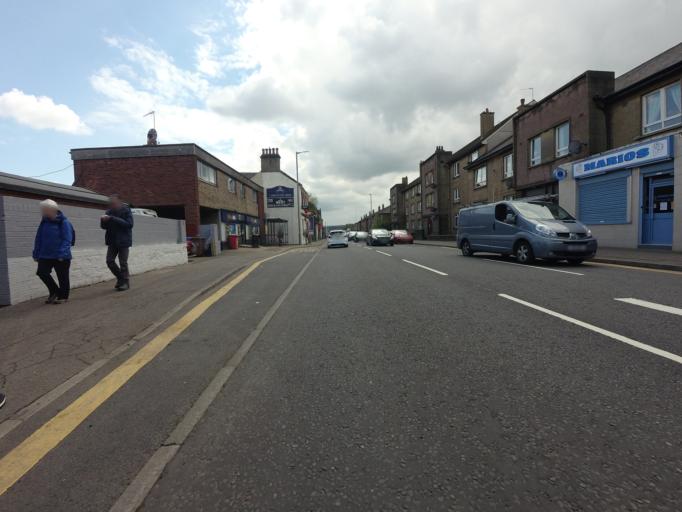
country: GB
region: Scotland
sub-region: Falkirk
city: Falkirk
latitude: 56.0134
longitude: -3.7889
